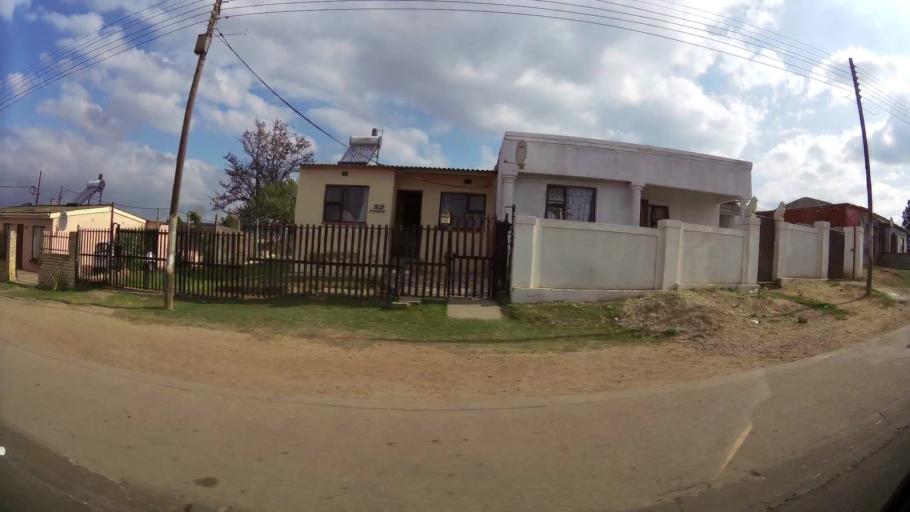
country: ZA
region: Eastern Cape
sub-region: Nelson Mandela Bay Metropolitan Municipality
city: Uitenhage
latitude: -33.7419
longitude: 25.3857
